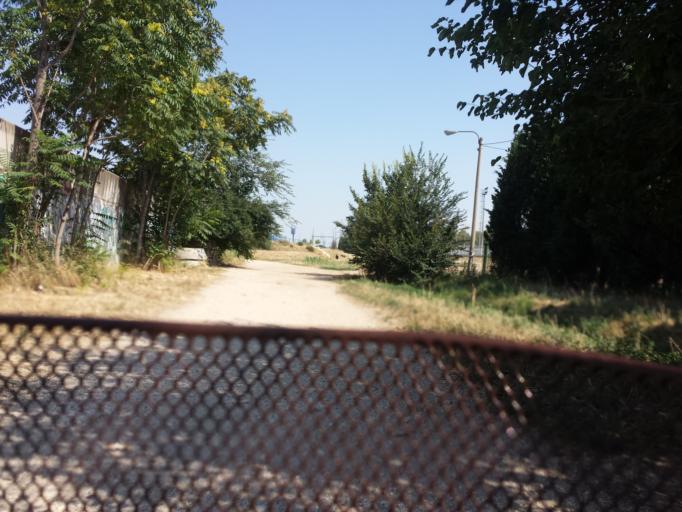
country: ES
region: Aragon
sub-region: Provincia de Zaragoza
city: Zaragoza
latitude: 41.6349
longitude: -0.8722
